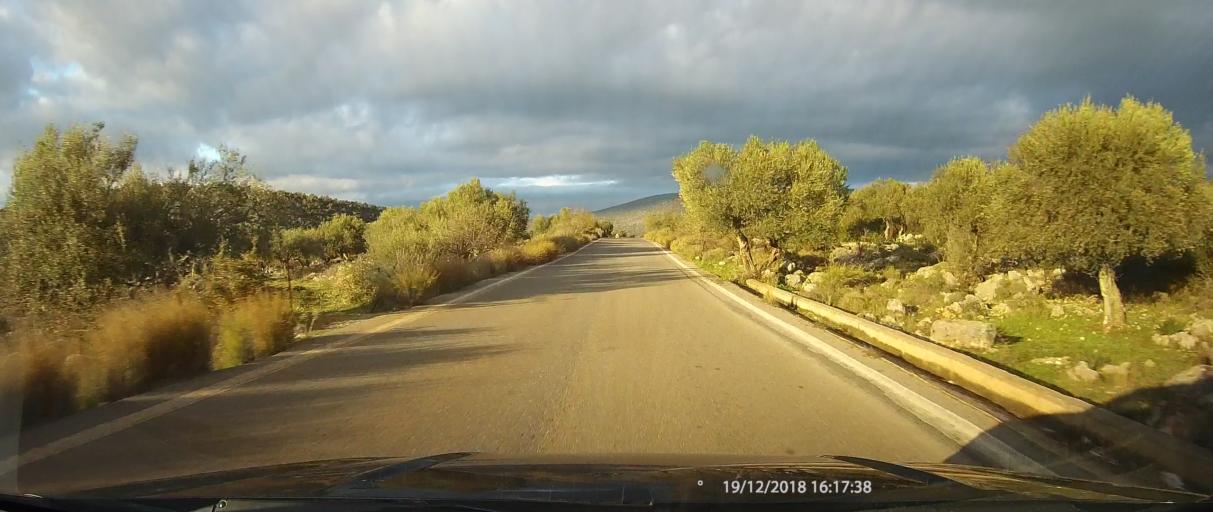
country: GR
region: Peloponnese
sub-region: Nomos Lakonias
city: Kato Glikovrisi
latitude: 36.9132
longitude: 22.8111
